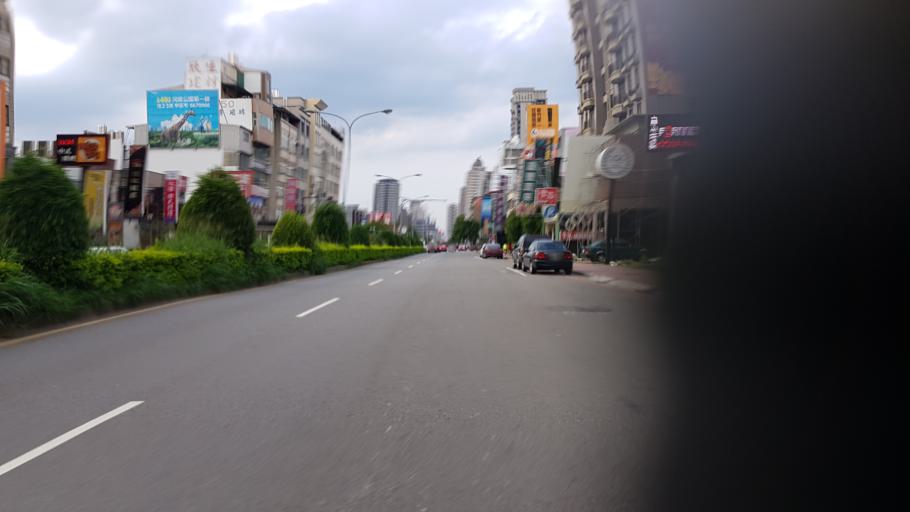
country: TW
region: Taiwan
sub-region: Hsinchu
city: Zhubei
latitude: 24.8121
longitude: 121.0257
